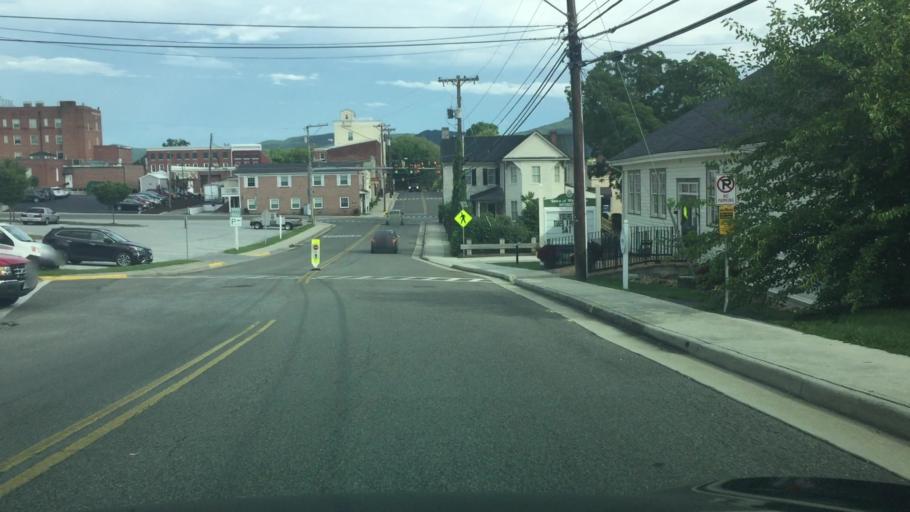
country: US
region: Virginia
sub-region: Wythe County
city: Wytheville
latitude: 36.9512
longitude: -81.0851
